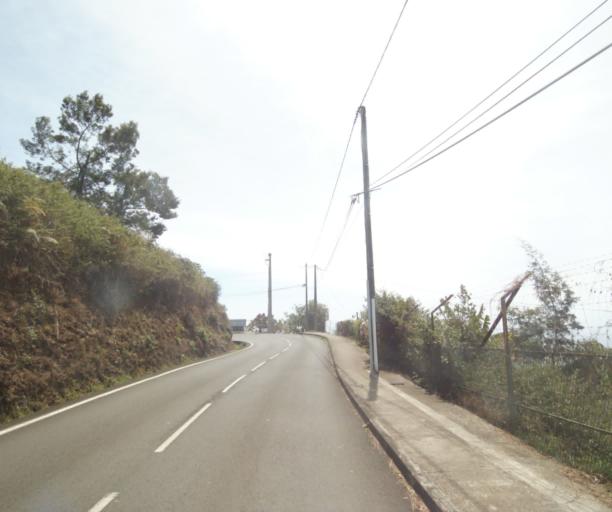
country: RE
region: Reunion
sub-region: Reunion
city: Trois-Bassins
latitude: -21.0593
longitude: 55.3085
